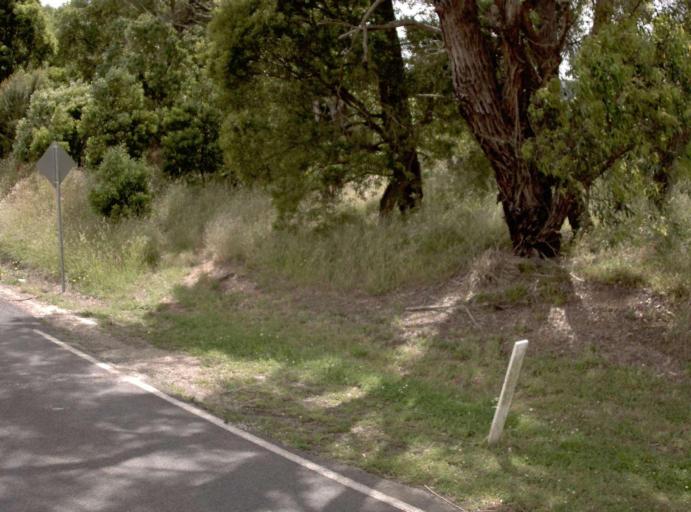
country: AU
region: Victoria
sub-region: Latrobe
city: Moe
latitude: -38.0919
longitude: 146.1567
